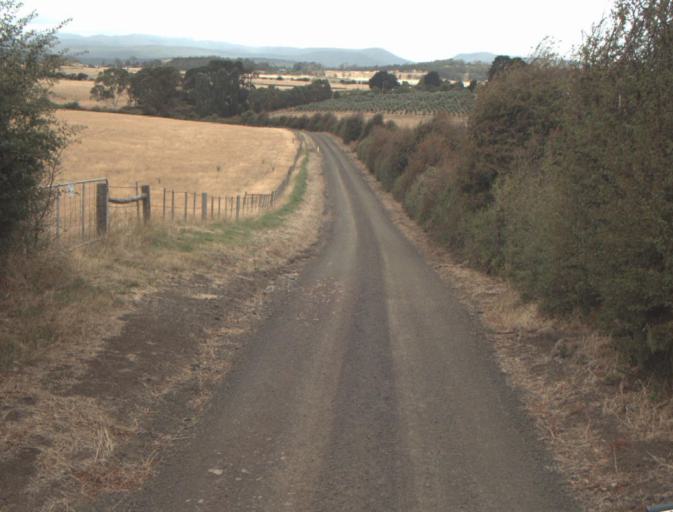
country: AU
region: Tasmania
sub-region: Northern Midlands
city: Evandale
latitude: -41.5278
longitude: 147.2755
